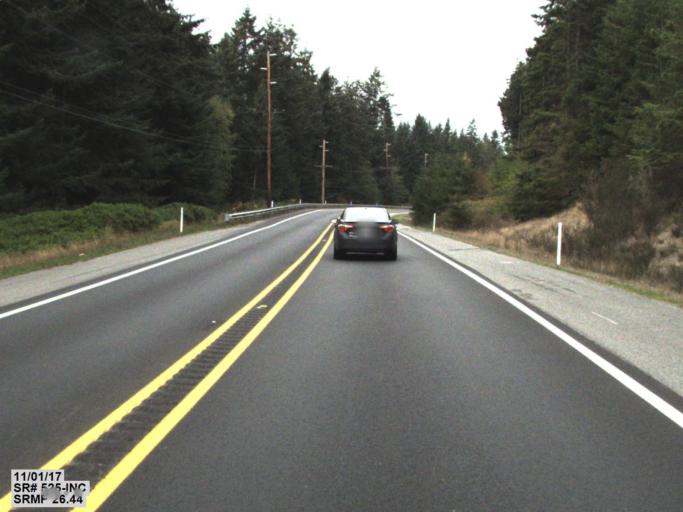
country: US
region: Washington
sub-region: Island County
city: Camano
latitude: 48.1158
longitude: -122.5854
